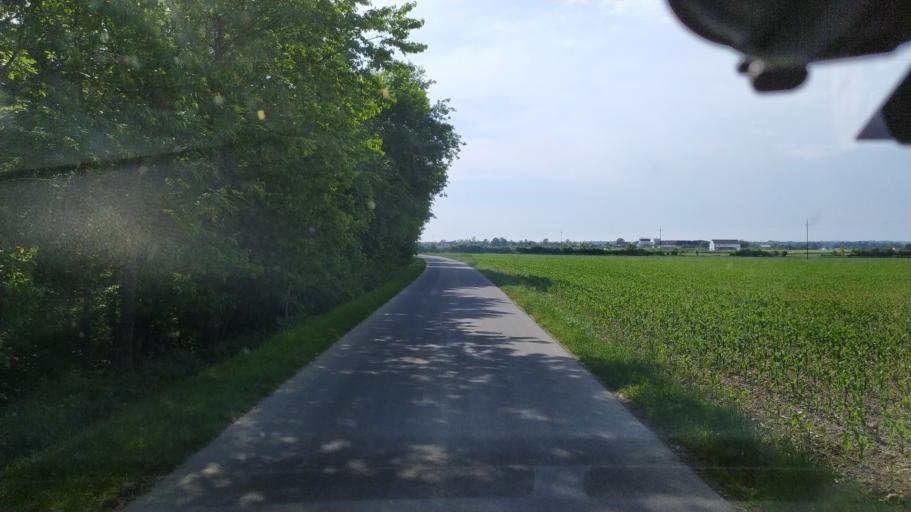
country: AT
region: Lower Austria
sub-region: Politischer Bezirk Amstetten
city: Zeillern
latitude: 48.1933
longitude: 14.7378
